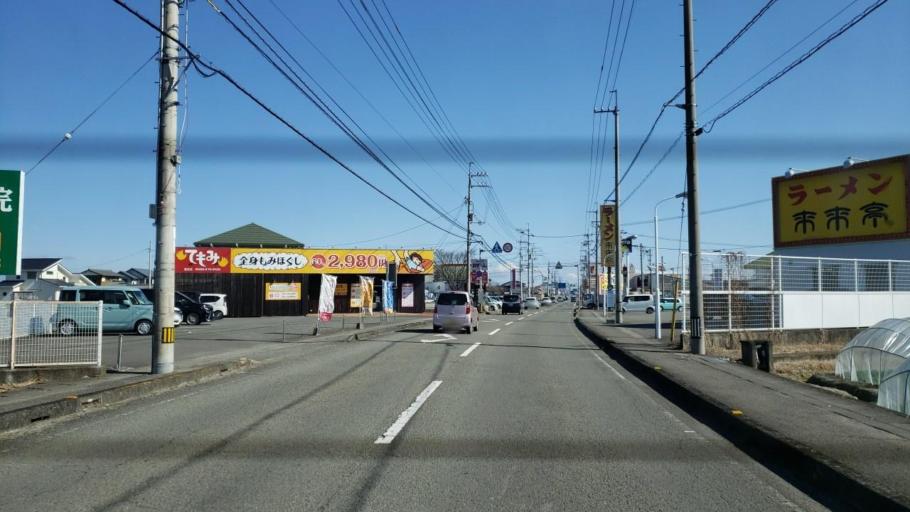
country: JP
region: Tokushima
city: Tokushima-shi
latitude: 34.1339
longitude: 134.5110
